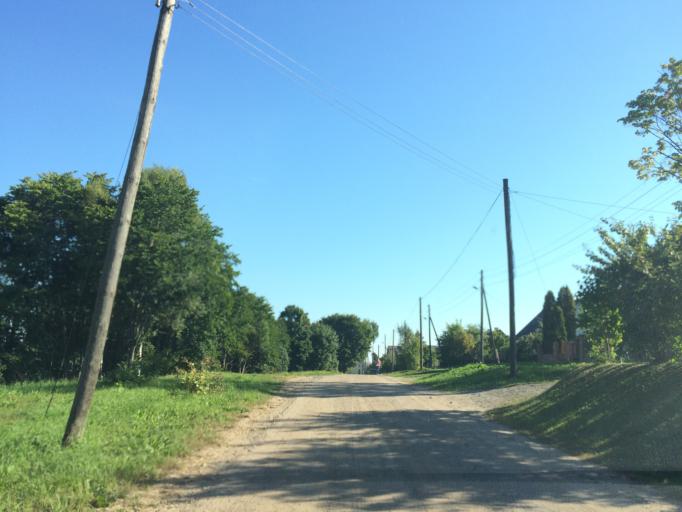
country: LV
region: Rezekne
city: Rezekne
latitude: 56.5083
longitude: 27.3497
